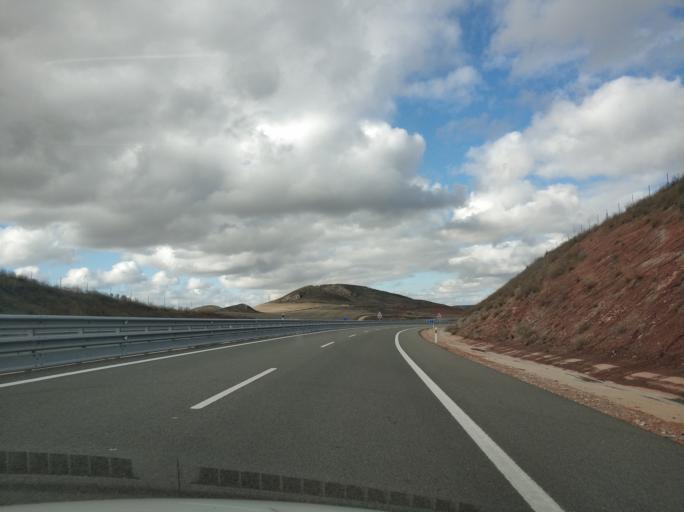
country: ES
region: Castille and Leon
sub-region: Provincia de Soria
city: Medinaceli
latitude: 41.1953
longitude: -2.4559
